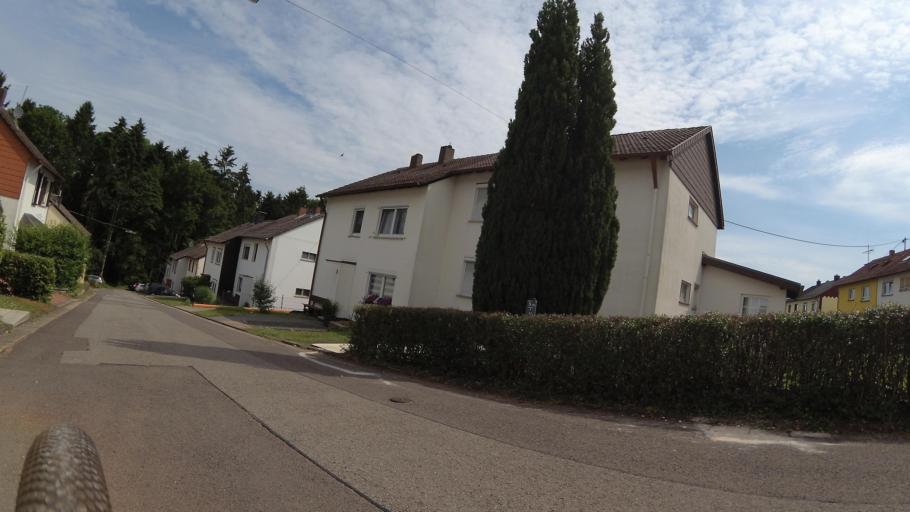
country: DE
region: Saarland
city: Friedrichsthal
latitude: 49.3587
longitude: 7.0896
